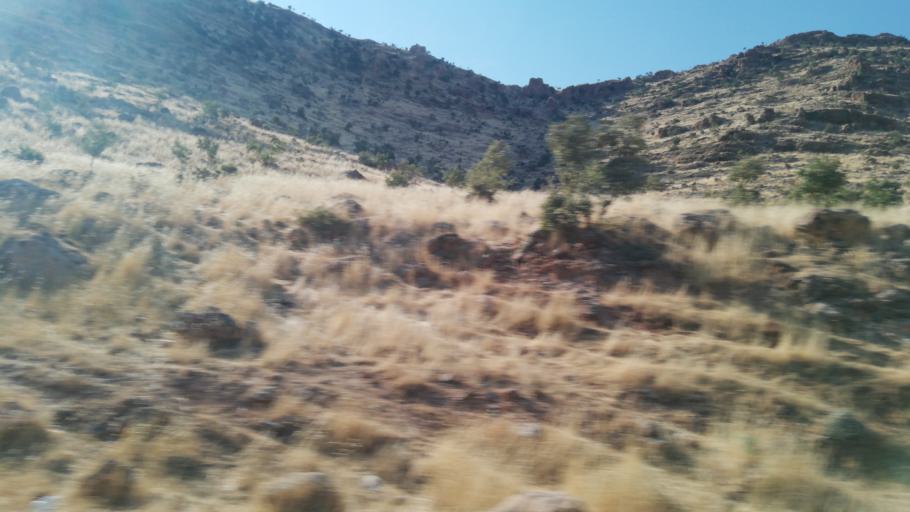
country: TR
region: Mardin
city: Sivrice
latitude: 37.2485
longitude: 41.3498
